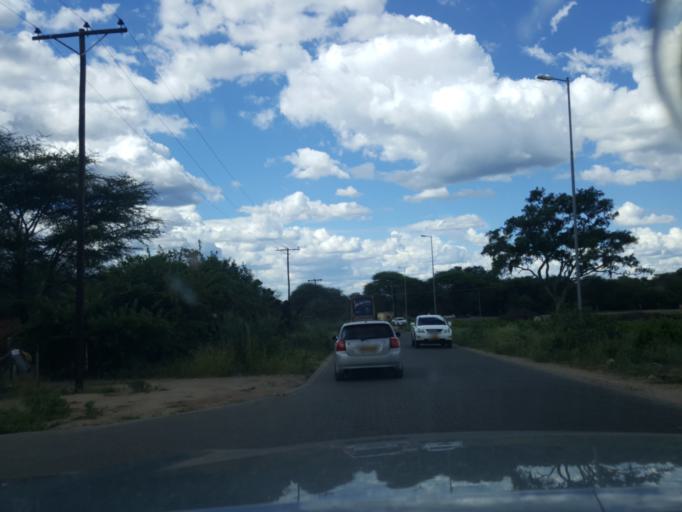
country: BW
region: North West
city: Kasane
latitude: -17.8039
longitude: 25.2403
